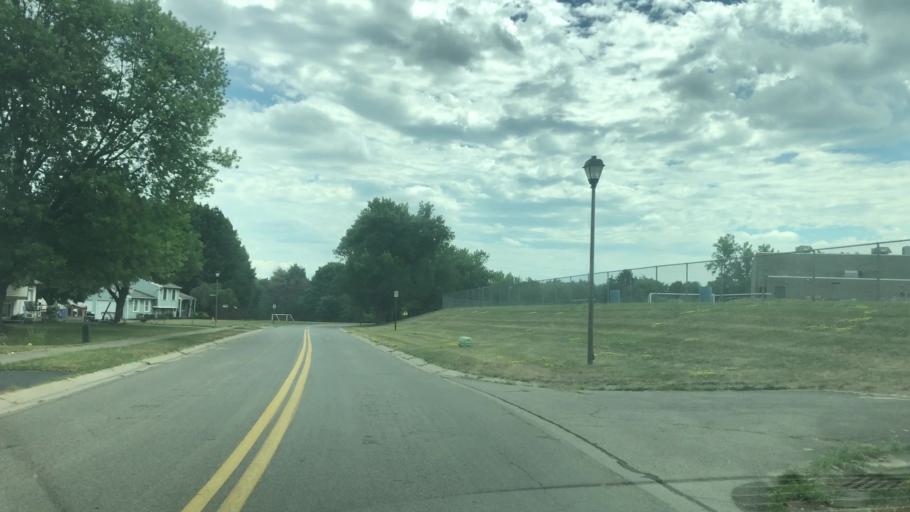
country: US
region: New York
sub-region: Wayne County
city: Macedon
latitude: 43.1271
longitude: -77.3073
